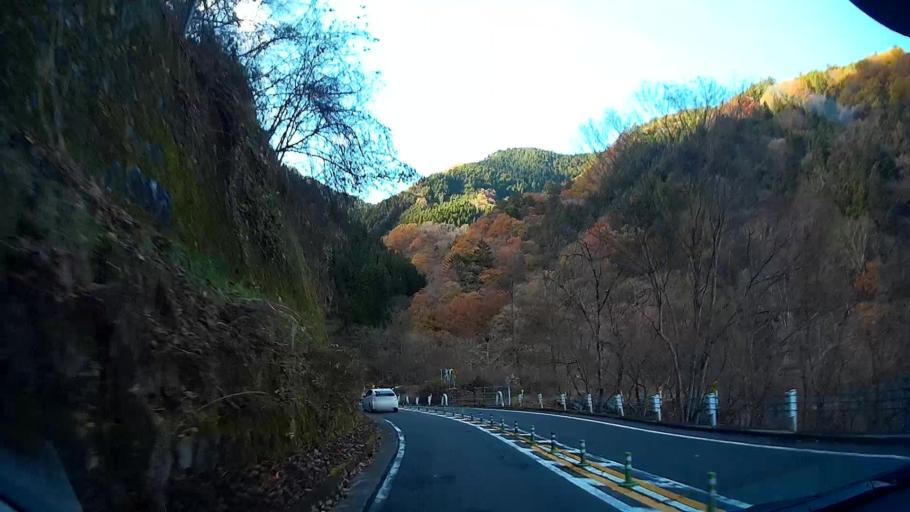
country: JP
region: Yamanashi
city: Uenohara
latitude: 35.7637
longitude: 139.0204
